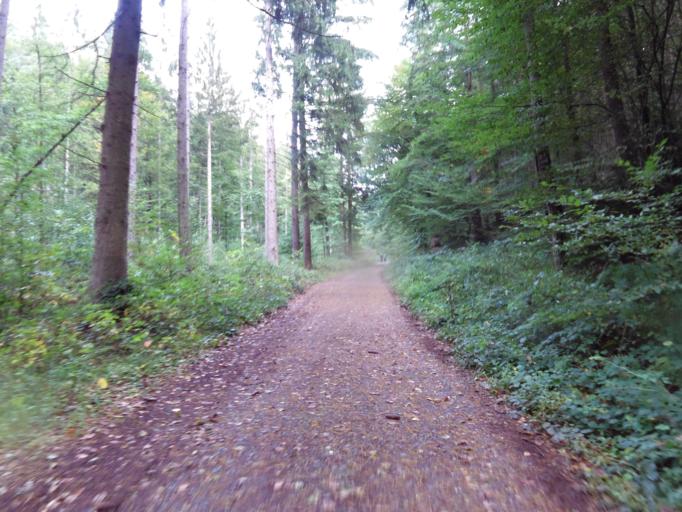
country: DE
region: Rheinland-Pfalz
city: Ramsen
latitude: 49.5068
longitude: 7.9777
